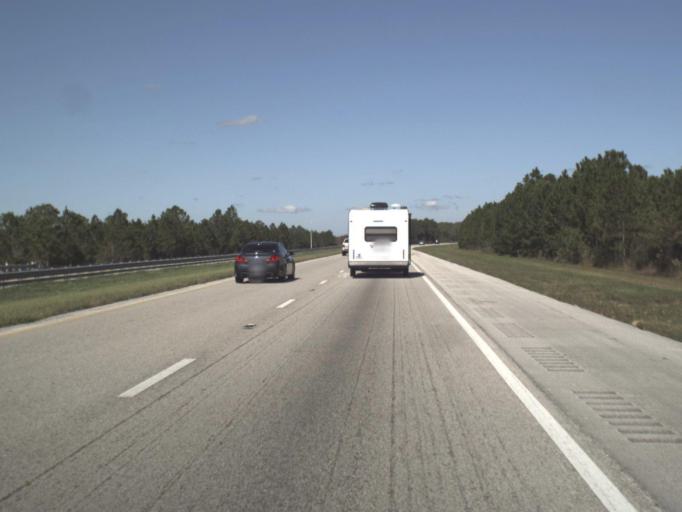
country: US
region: Florida
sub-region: Osceola County
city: Saint Cloud
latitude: 27.9576
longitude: -81.0959
